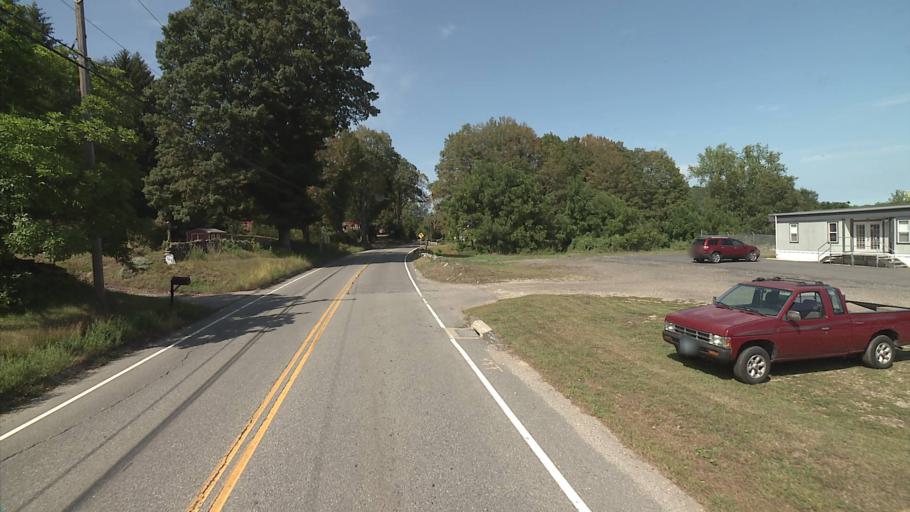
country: US
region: Connecticut
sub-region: New London County
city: Baltic
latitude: 41.5758
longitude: -72.1382
